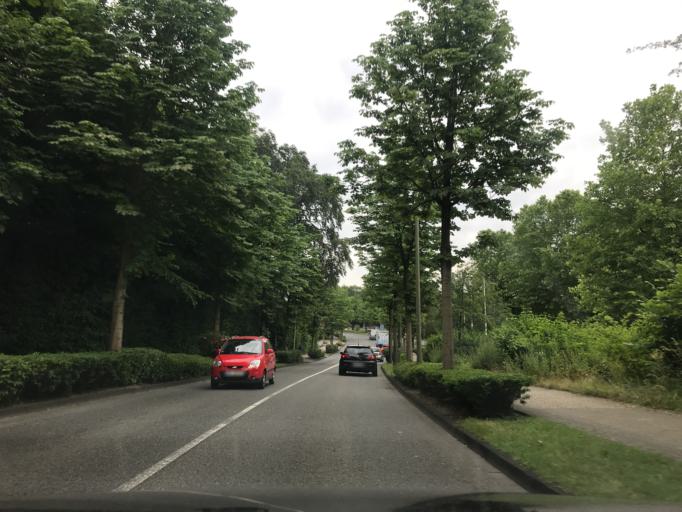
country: DE
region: North Rhine-Westphalia
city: Haan
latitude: 51.1923
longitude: 6.9976
